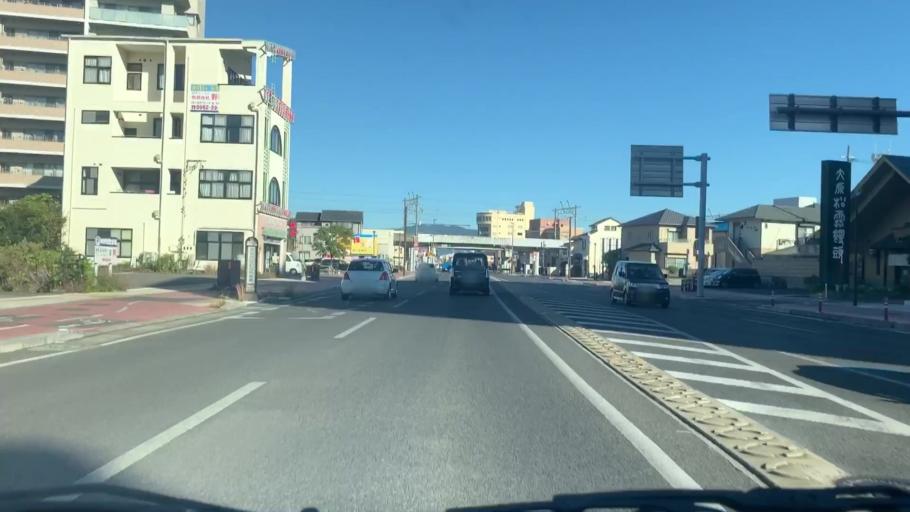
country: JP
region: Saga Prefecture
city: Saga-shi
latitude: 33.2619
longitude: 130.2933
